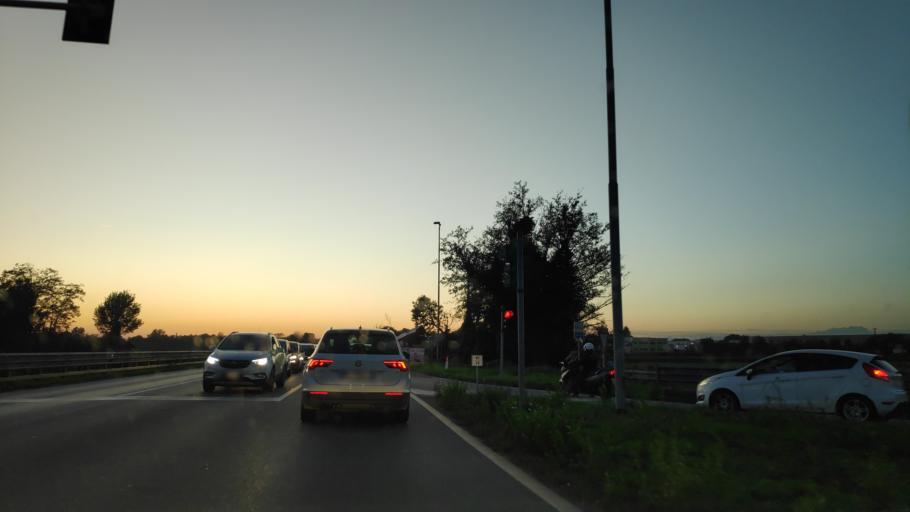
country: IT
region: Lombardy
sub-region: Citta metropolitana di Milano
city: Vermezzo
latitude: 45.4025
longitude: 8.9695
